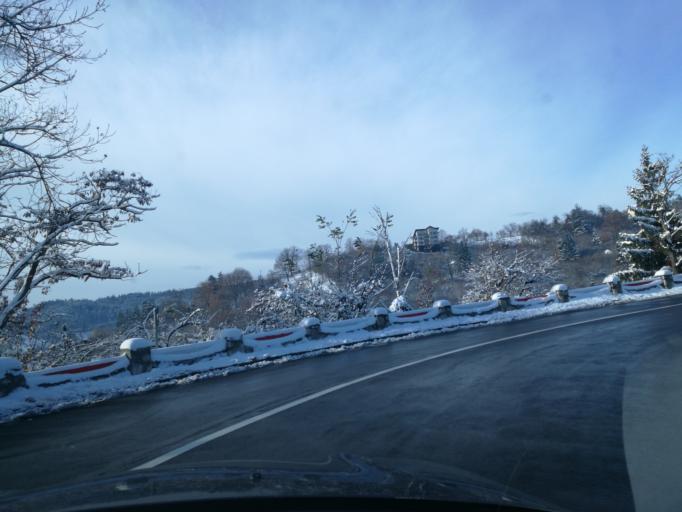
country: RO
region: Brasov
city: Brasov
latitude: 45.6421
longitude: 25.5844
